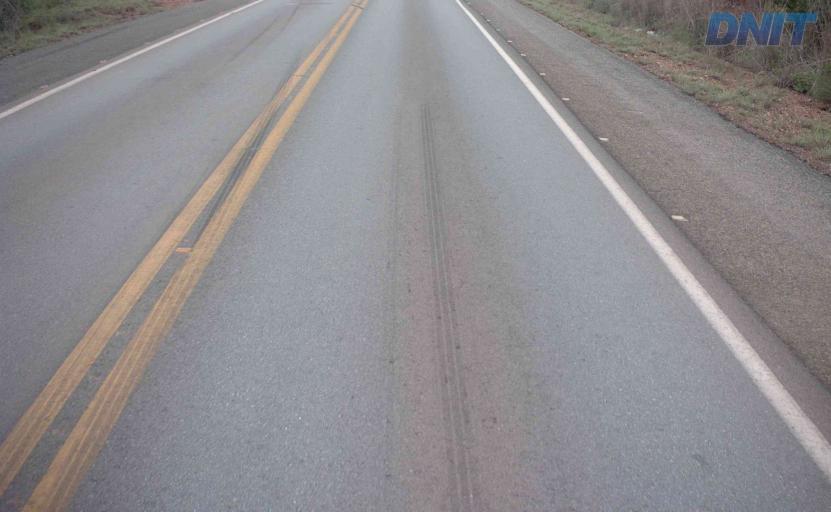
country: BR
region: Goias
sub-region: Barro Alto
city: Barro Alto
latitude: -14.7645
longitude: -49.0610
